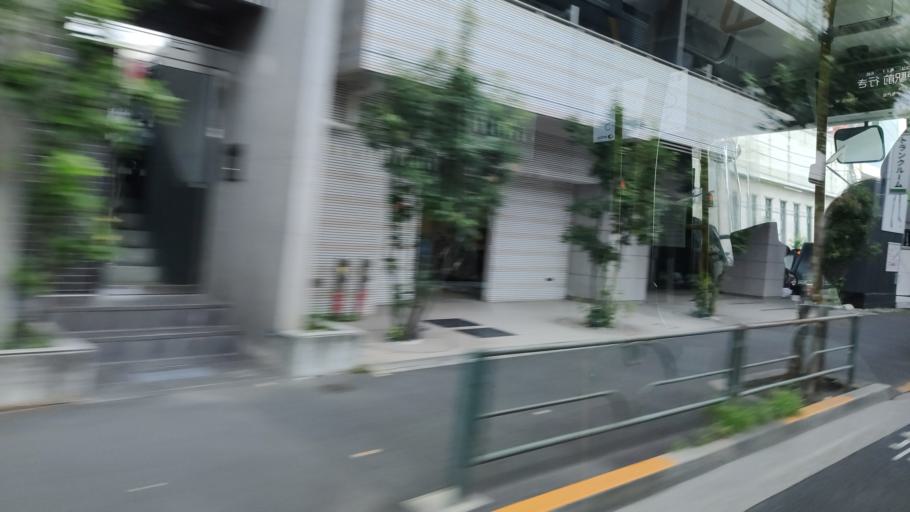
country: JP
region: Tokyo
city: Urayasu
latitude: 35.6780
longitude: 139.8343
